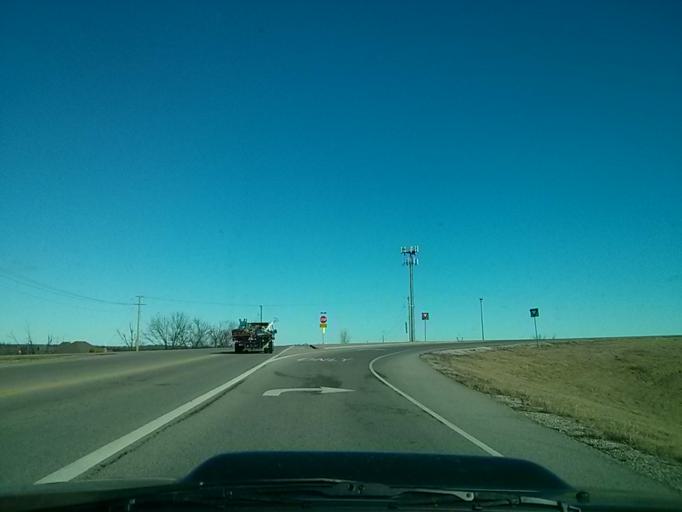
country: US
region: Oklahoma
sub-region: Tulsa County
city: Glenpool
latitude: 36.0023
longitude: -96.0136
